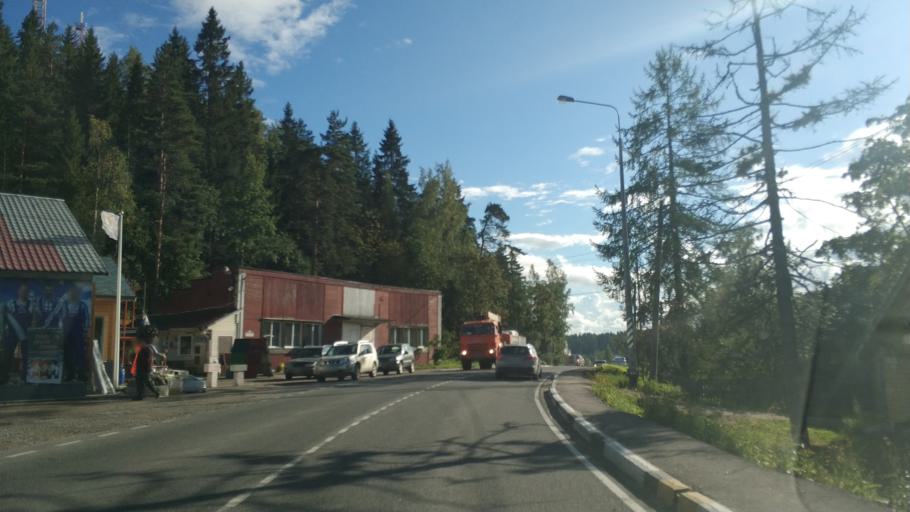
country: RU
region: Republic of Karelia
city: Lakhdenpokh'ya
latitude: 61.5255
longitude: 30.2015
